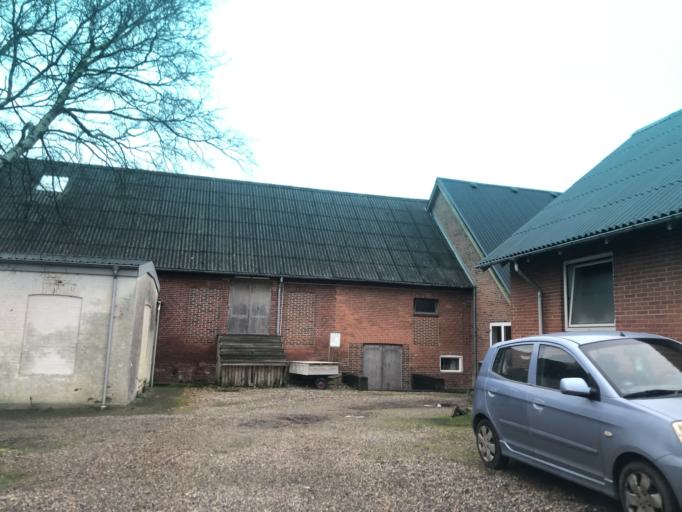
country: DK
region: North Denmark
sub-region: Thisted Kommune
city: Hurup
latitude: 56.7491
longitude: 8.4210
